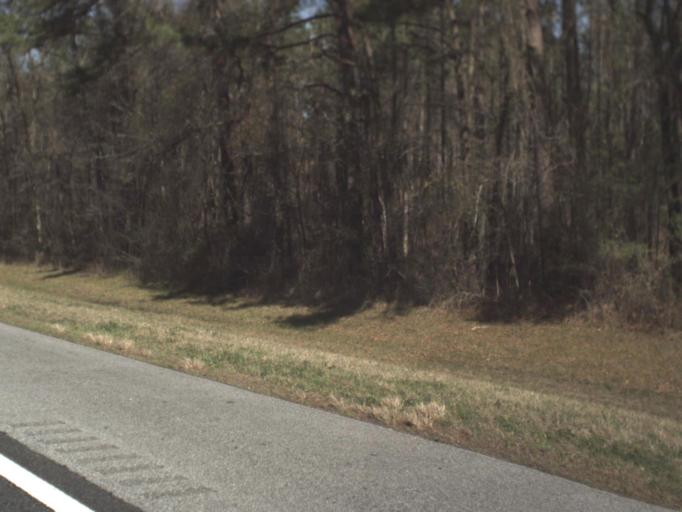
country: US
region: Florida
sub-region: Jackson County
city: Sneads
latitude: 30.6385
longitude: -84.9558
